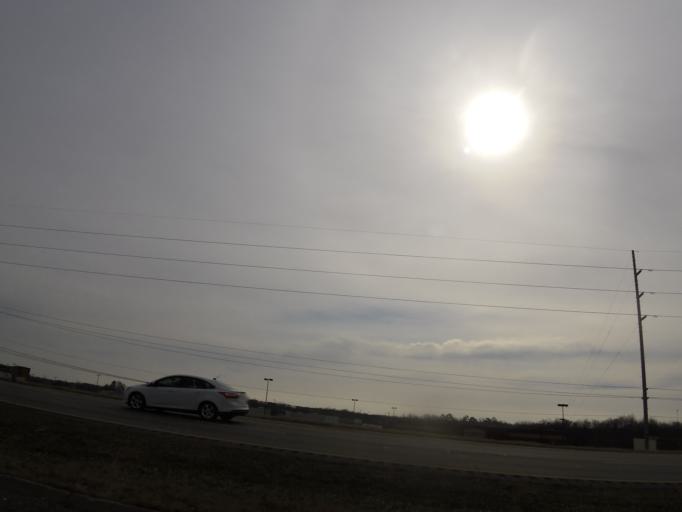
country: US
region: Alabama
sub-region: Montgomery County
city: Montgomery
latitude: 32.3282
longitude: -86.2354
